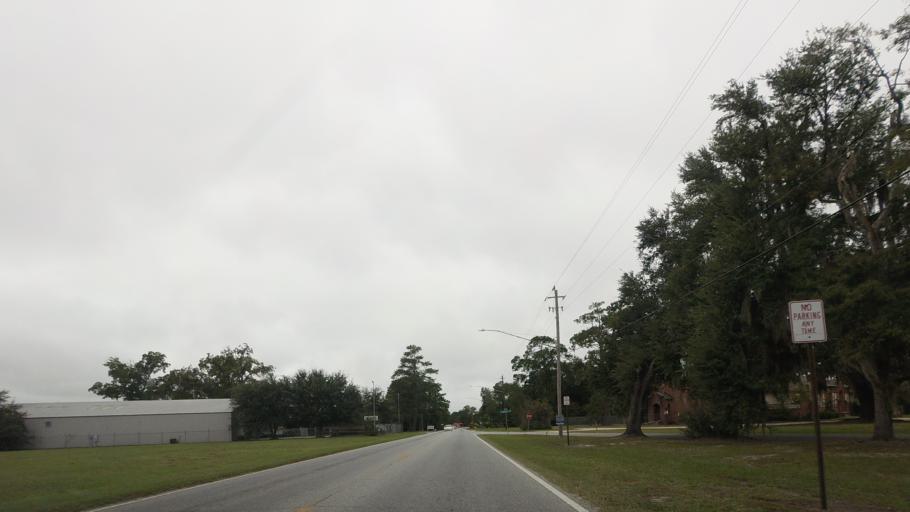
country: US
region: Georgia
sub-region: Lowndes County
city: Valdosta
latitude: 30.8195
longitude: -83.2685
